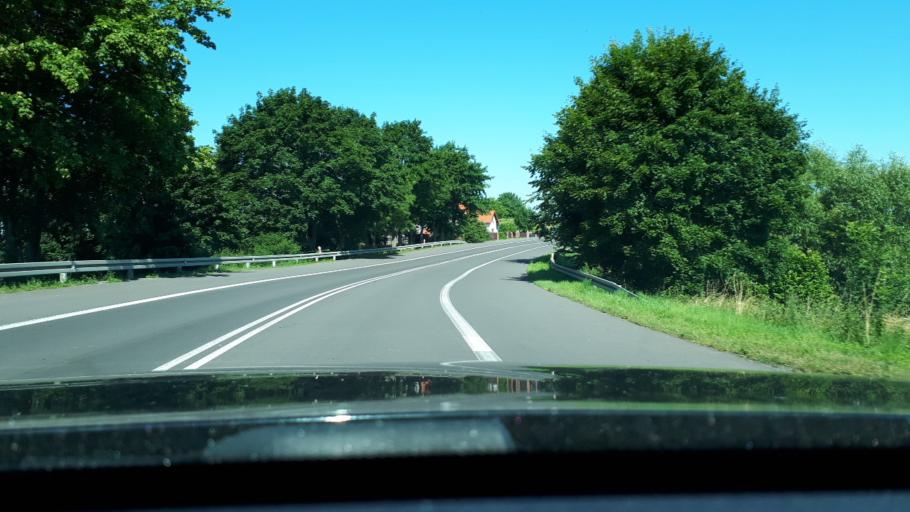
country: PL
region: Warmian-Masurian Voivodeship
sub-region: Powiat ostrodzki
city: Ostroda
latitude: 53.6639
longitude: 20.0411
